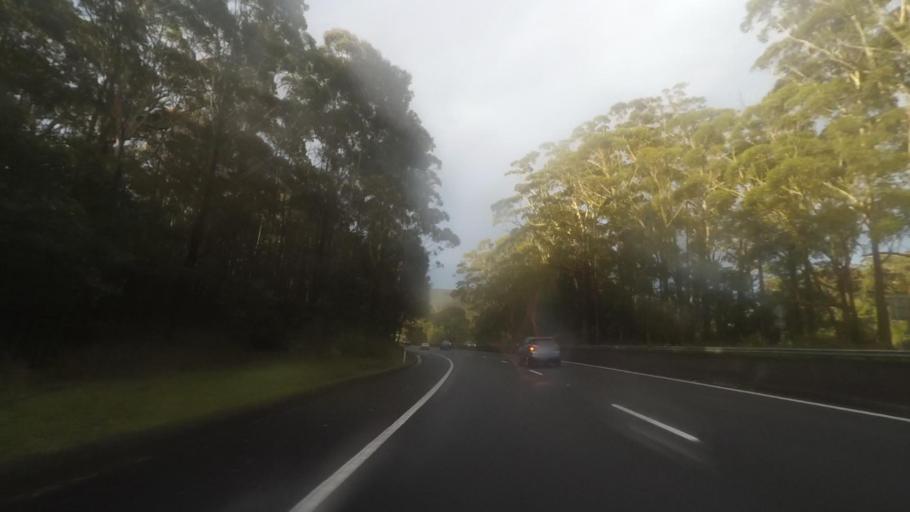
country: AU
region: New South Wales
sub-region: Wollongong
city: Bulli
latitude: -34.3435
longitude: 150.8770
